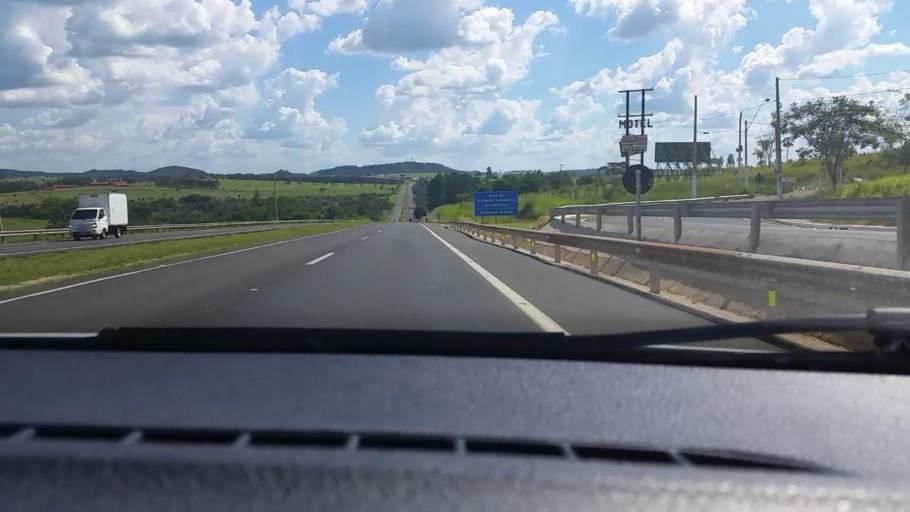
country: BR
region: Sao Paulo
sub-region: Bauru
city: Bauru
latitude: -22.4009
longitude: -49.0913
